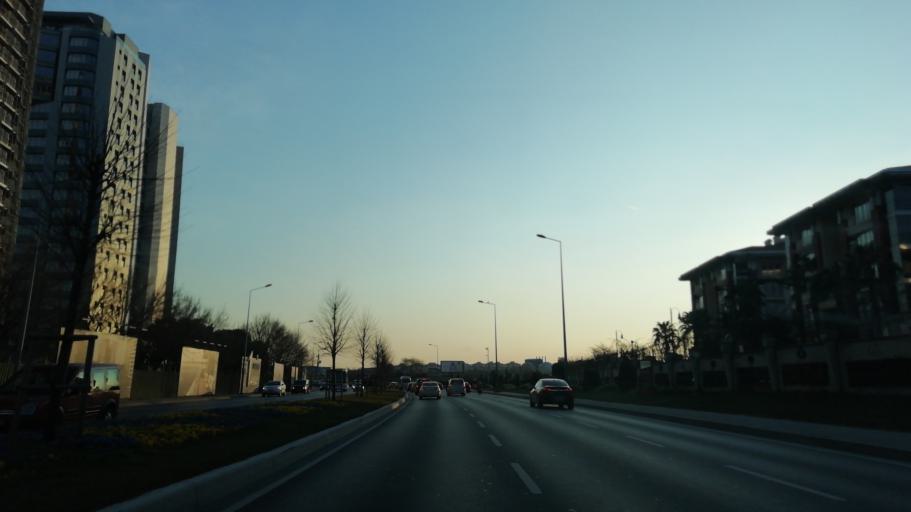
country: TR
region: Istanbul
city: Bahcelievler
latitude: 40.9751
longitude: 28.8490
